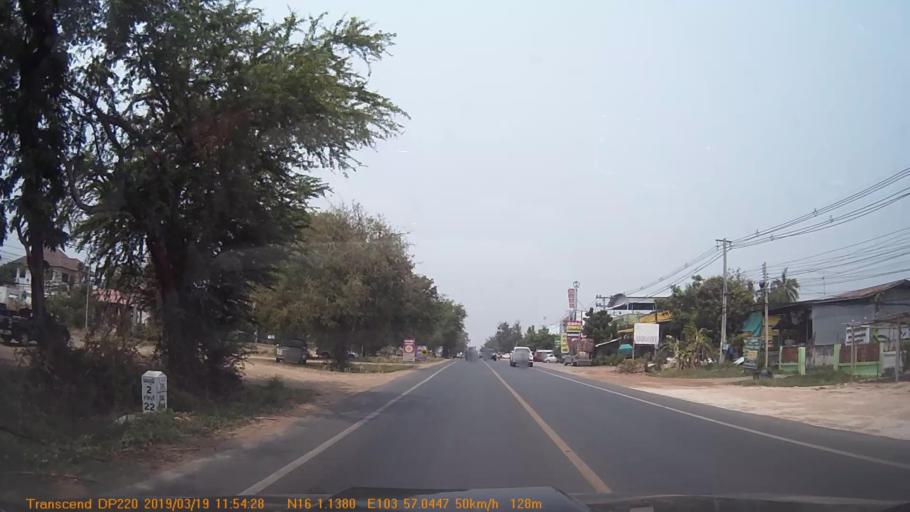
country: TH
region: Roi Et
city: Ban Selaphum
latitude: 16.0191
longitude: 103.9506
